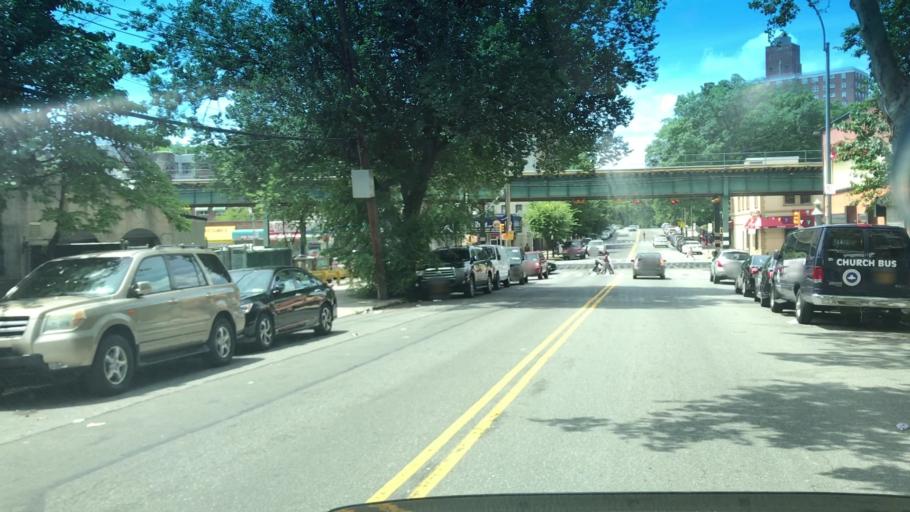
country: US
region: New York
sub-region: Bronx
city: The Bronx
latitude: 40.8679
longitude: -73.8663
